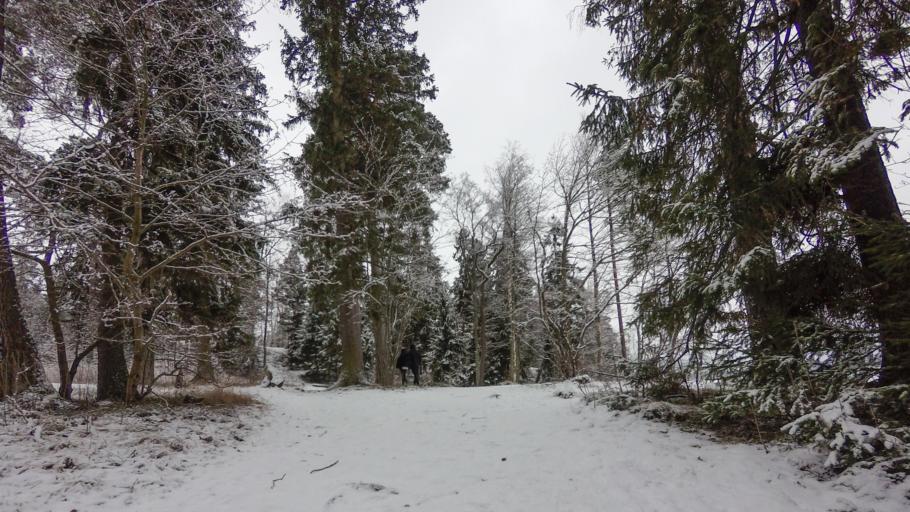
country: FI
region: Uusimaa
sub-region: Helsinki
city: Teekkarikylae
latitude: 60.1847
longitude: 24.8825
